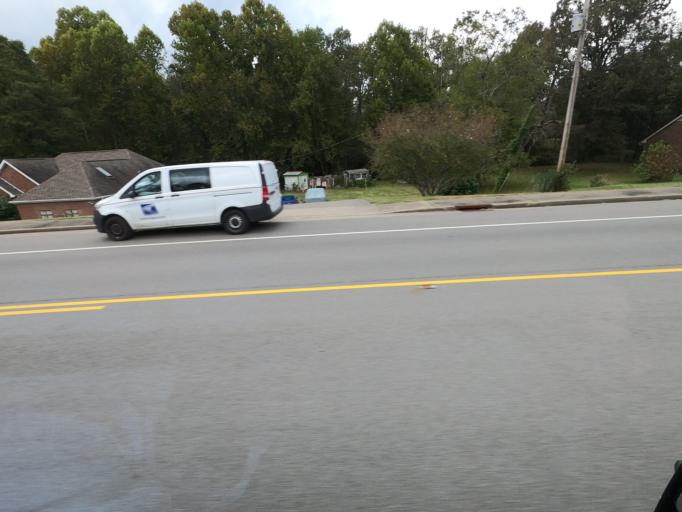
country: US
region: Tennessee
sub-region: Cheatham County
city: Kingston Springs
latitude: 36.0961
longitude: -87.0916
